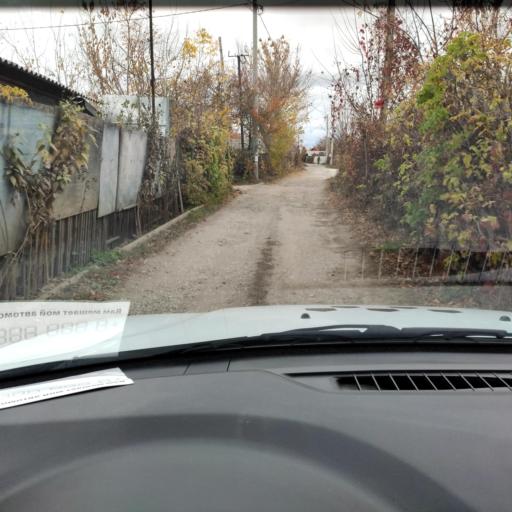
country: RU
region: Samara
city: Tol'yatti
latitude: 53.5379
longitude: 49.4308
